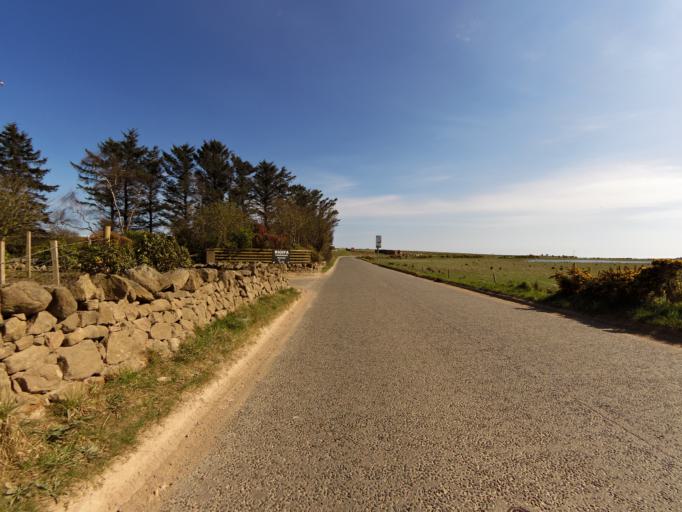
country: GB
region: Scotland
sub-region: Aberdeenshire
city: Portlethen
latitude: 57.0918
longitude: -2.0988
